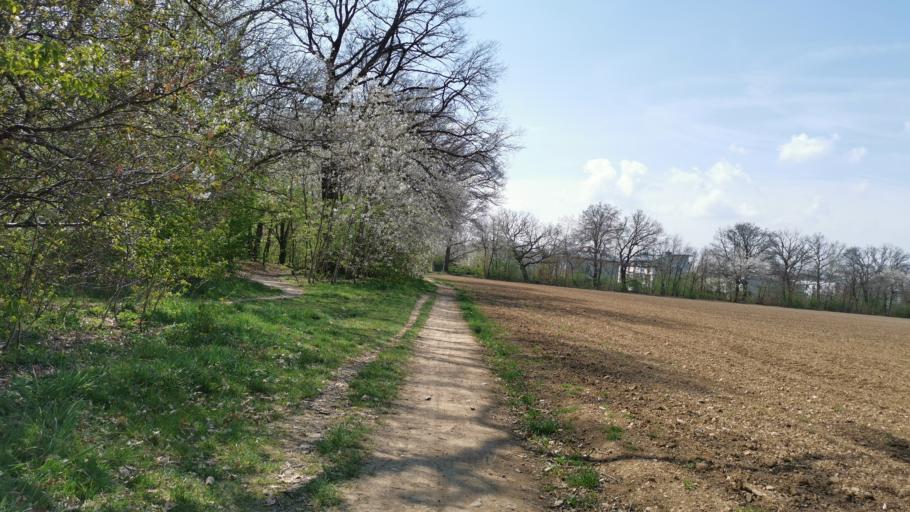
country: DE
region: Bavaria
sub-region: Upper Bavaria
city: Pullach im Isartal
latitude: 48.0880
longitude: 11.5297
